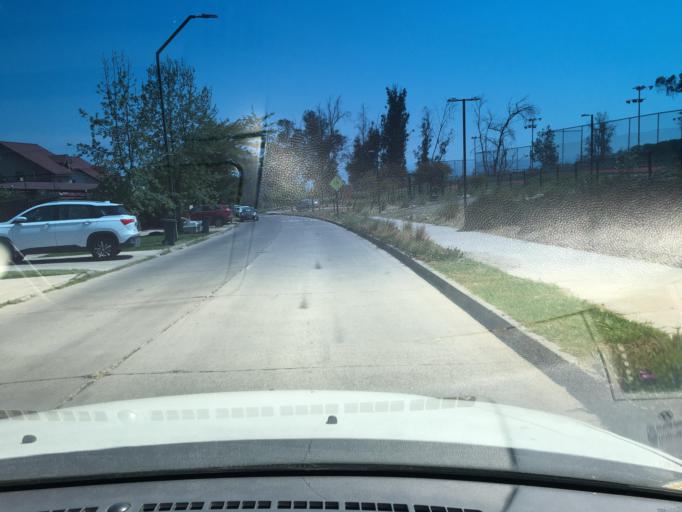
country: CL
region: Santiago Metropolitan
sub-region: Provincia de Santiago
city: Villa Presidente Frei, Nunoa, Santiago, Chile
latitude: -33.5113
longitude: -70.5330
